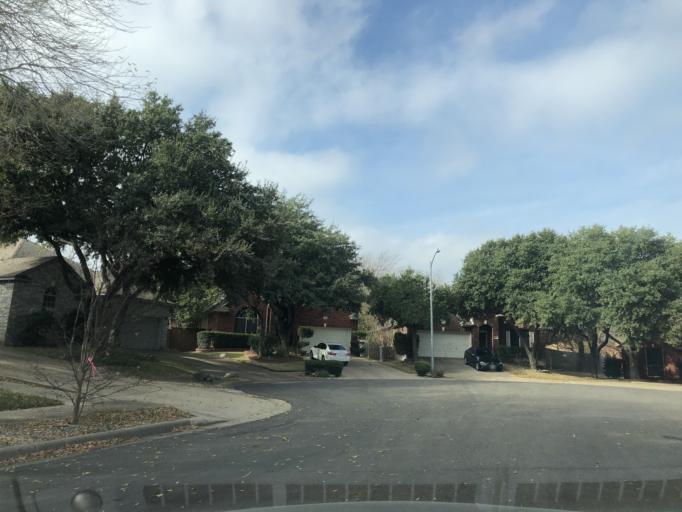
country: US
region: Texas
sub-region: Travis County
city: Wells Branch
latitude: 30.4199
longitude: -97.6848
